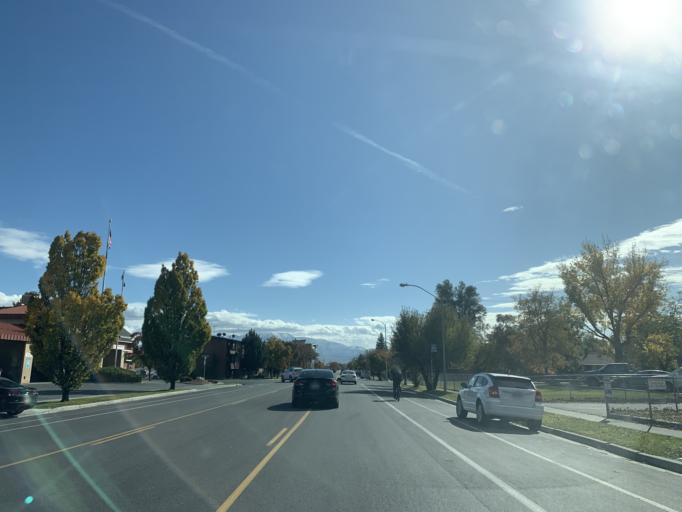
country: US
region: Utah
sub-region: Utah County
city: Provo
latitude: 40.2291
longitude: -111.6623
